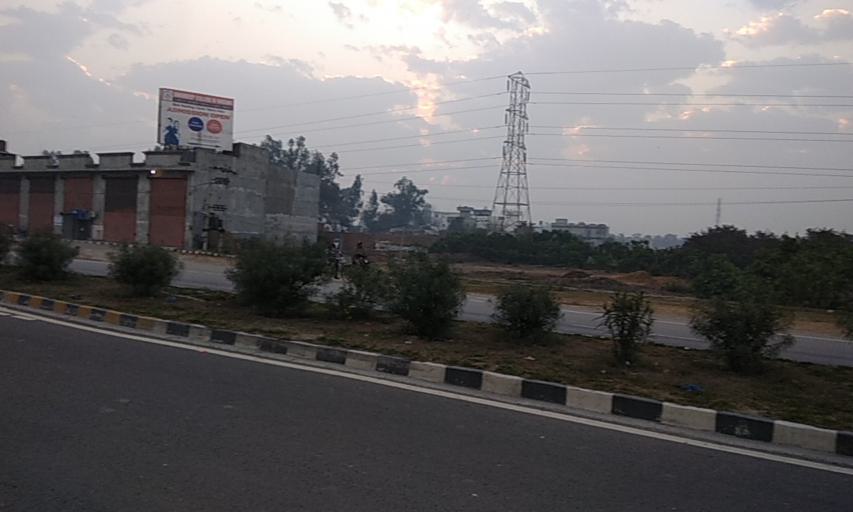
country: IN
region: Punjab
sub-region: Amritsar
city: Majitha
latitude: 31.6957
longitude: 74.9828
